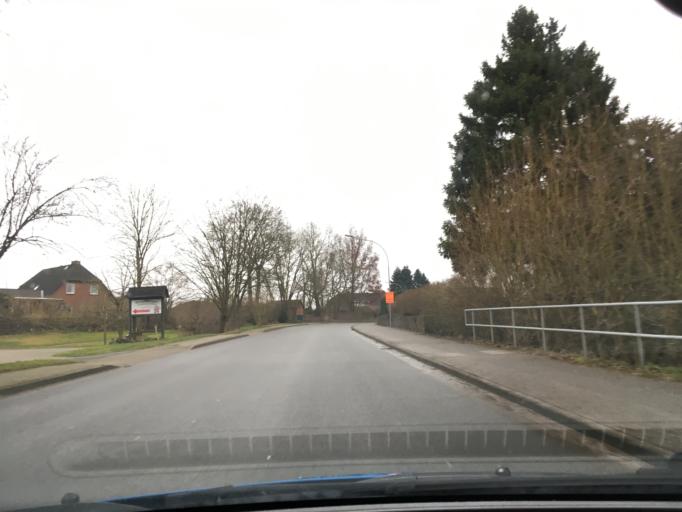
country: DE
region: Schleswig-Holstein
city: Roseburg
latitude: 53.5312
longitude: 10.6250
